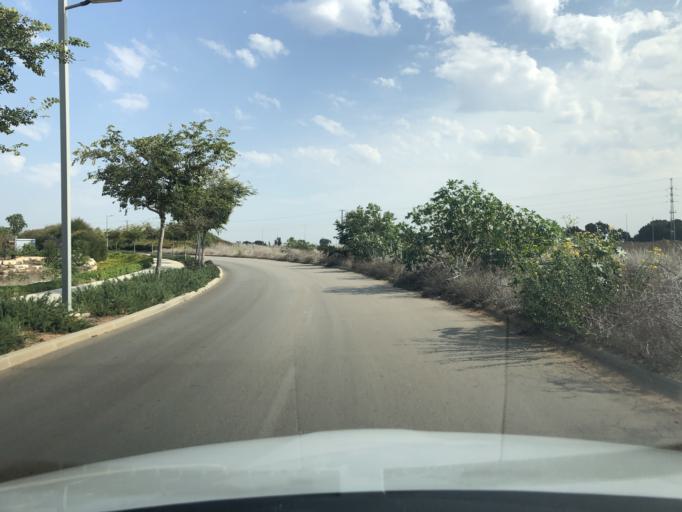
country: IL
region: Tel Aviv
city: Kefar Shemaryahu
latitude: 32.2129
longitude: 34.8244
